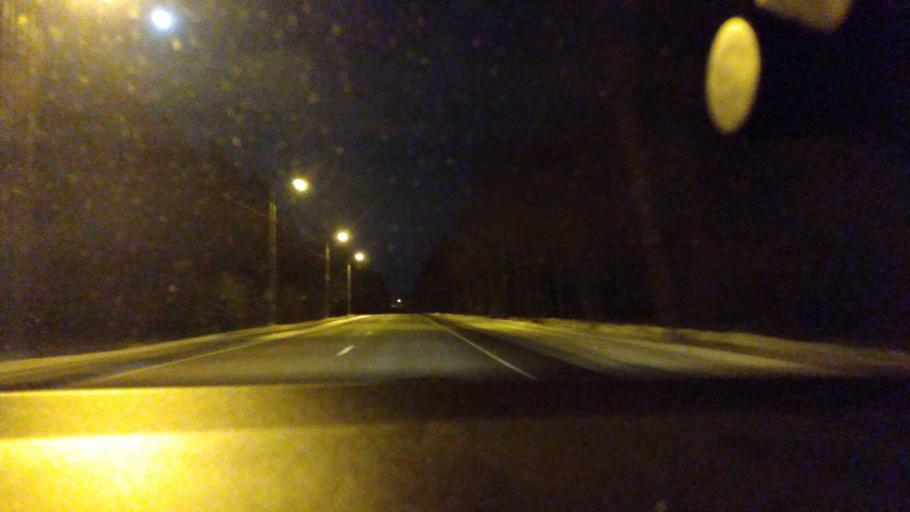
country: RU
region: Moskovskaya
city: Il'inskiy Pogost
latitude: 55.4830
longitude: 38.9288
